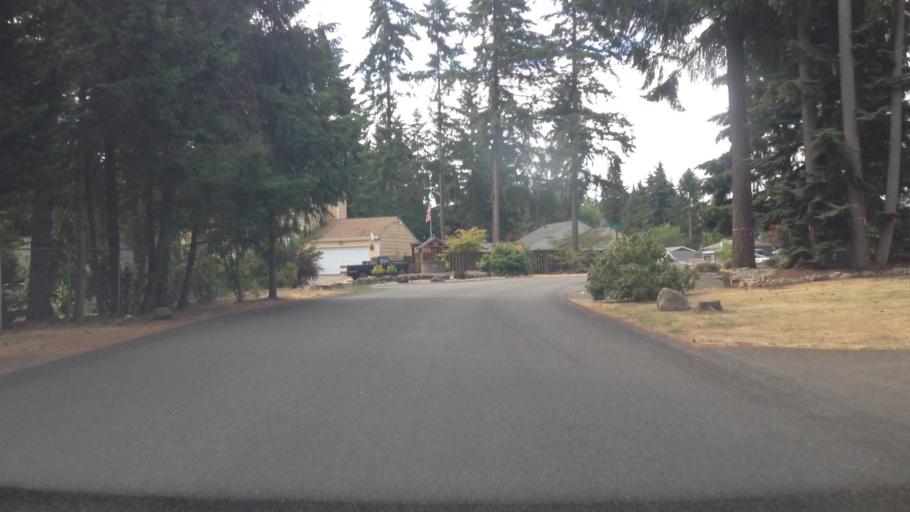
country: US
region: Washington
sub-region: Pierce County
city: South Hill
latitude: 47.1142
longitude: -122.3021
